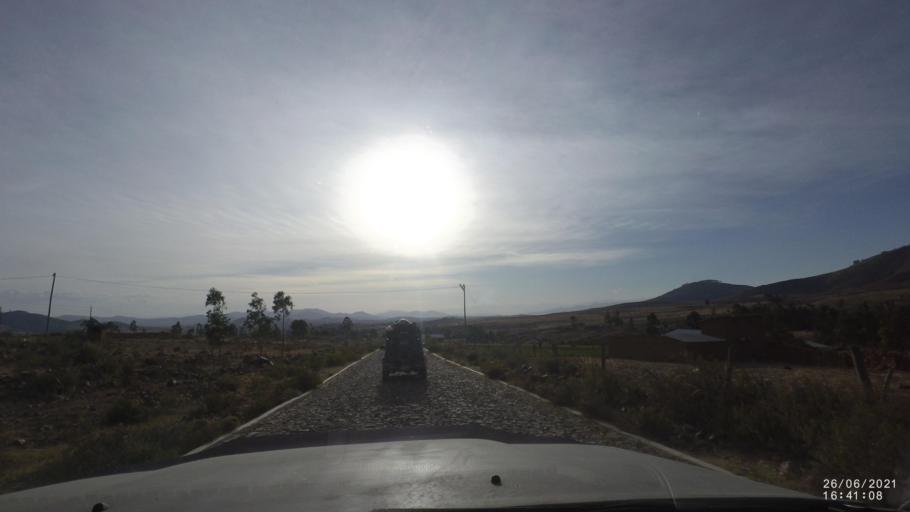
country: BO
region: Cochabamba
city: Arani
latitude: -17.7681
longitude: -65.8181
